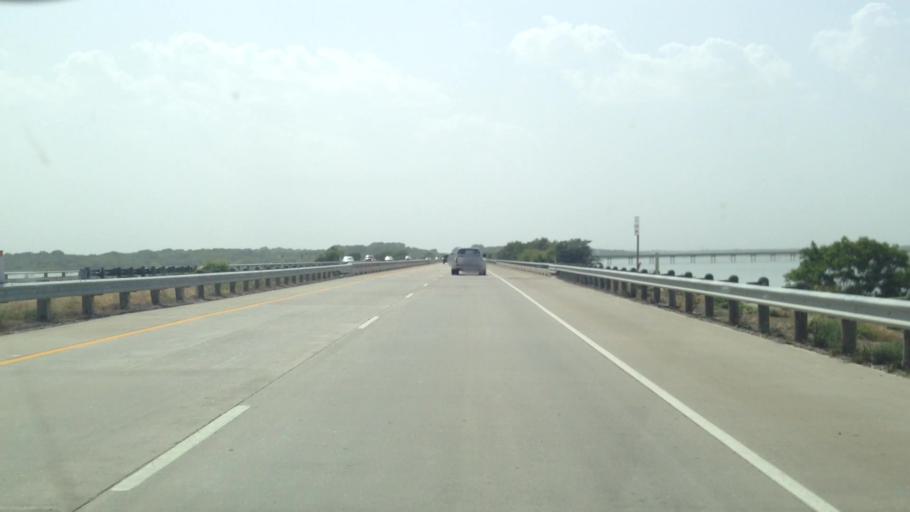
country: US
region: Texas
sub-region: Collin County
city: Farmersville
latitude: 33.1615
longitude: -96.4224
